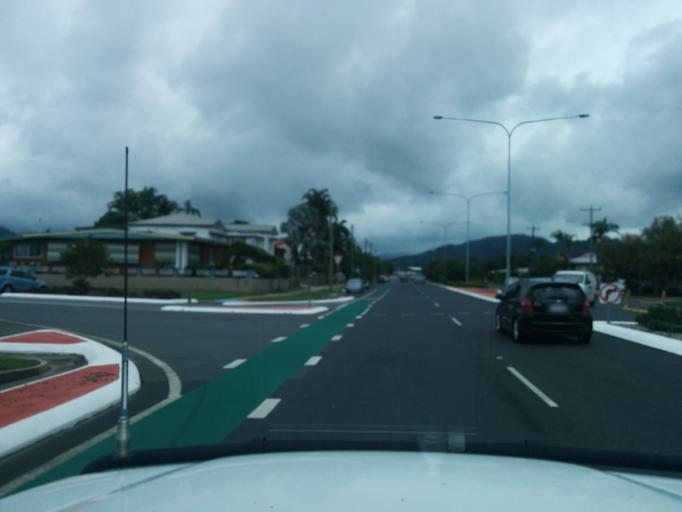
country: AU
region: Queensland
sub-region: Cairns
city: Cairns
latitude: -16.9280
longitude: 145.7563
